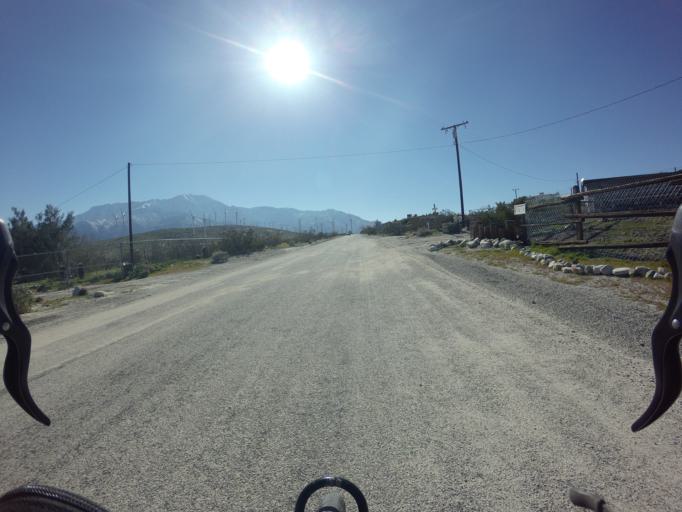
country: US
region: California
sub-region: Riverside County
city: Garnet
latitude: 33.9363
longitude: -116.6071
